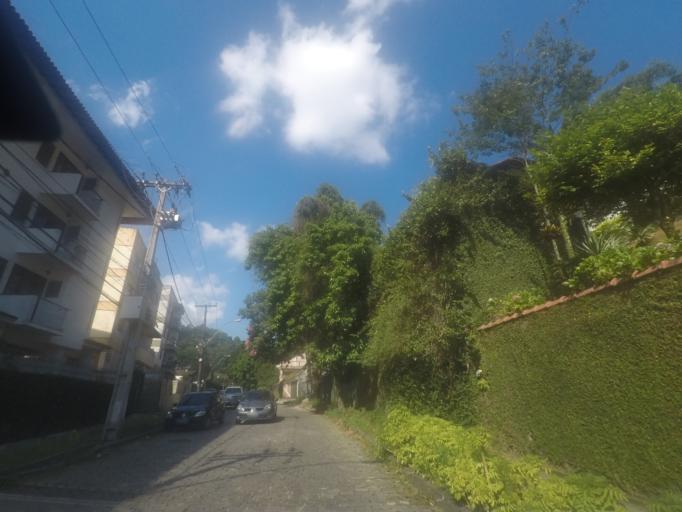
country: BR
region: Rio de Janeiro
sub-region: Petropolis
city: Petropolis
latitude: -22.5251
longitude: -43.2110
